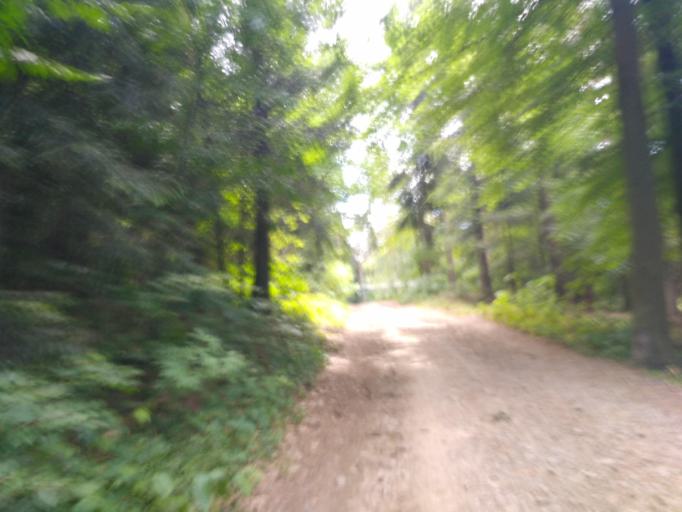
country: PL
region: Subcarpathian Voivodeship
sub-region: Powiat jasielski
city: Brzyska
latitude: 49.8061
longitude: 21.3651
